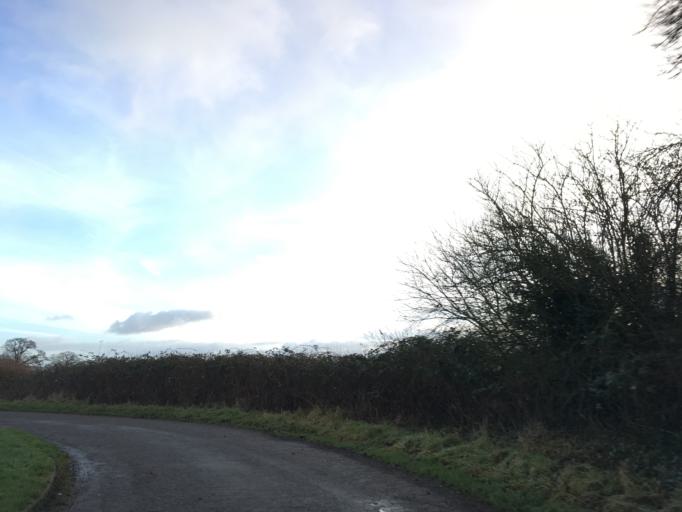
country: GB
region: England
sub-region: South Gloucestershire
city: Falfield
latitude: 51.6528
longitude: -2.4574
